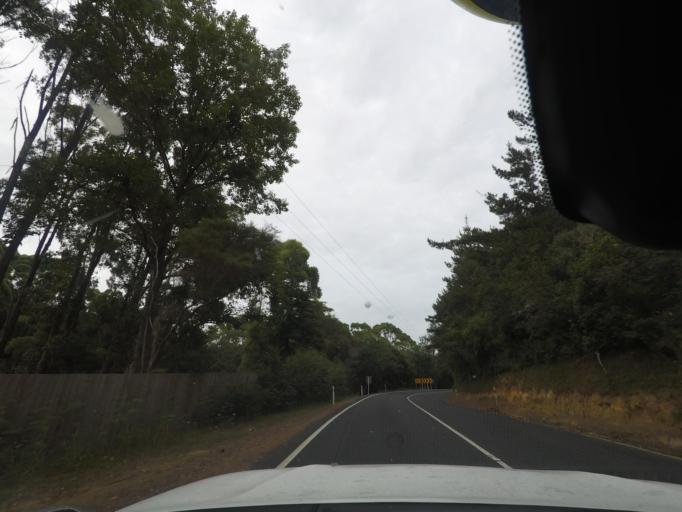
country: NZ
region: Auckland
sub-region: Auckland
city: Parakai
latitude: -36.5215
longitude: 174.2758
